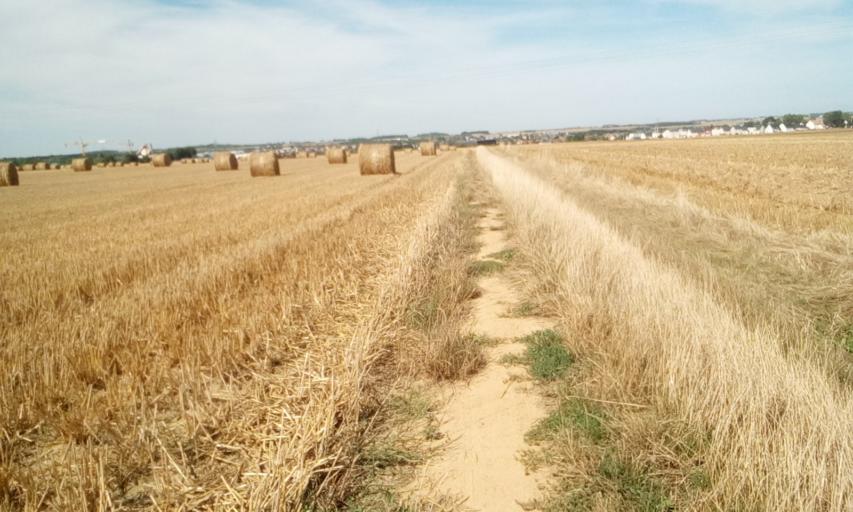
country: FR
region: Lower Normandy
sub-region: Departement du Calvados
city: Fontaine-Etoupefour
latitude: 49.1329
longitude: -0.4547
